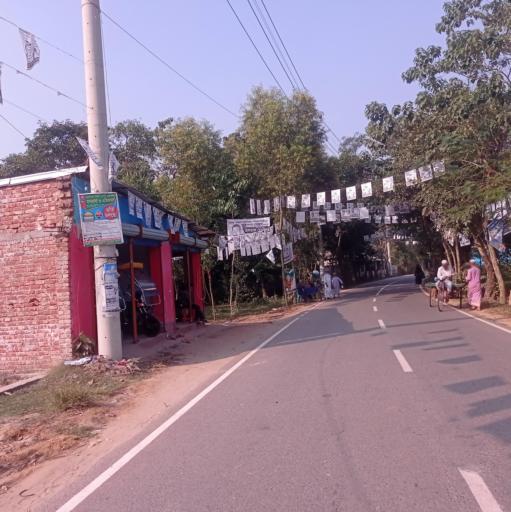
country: BD
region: Dhaka
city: Bhairab Bazar
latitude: 24.0373
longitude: 90.8321
